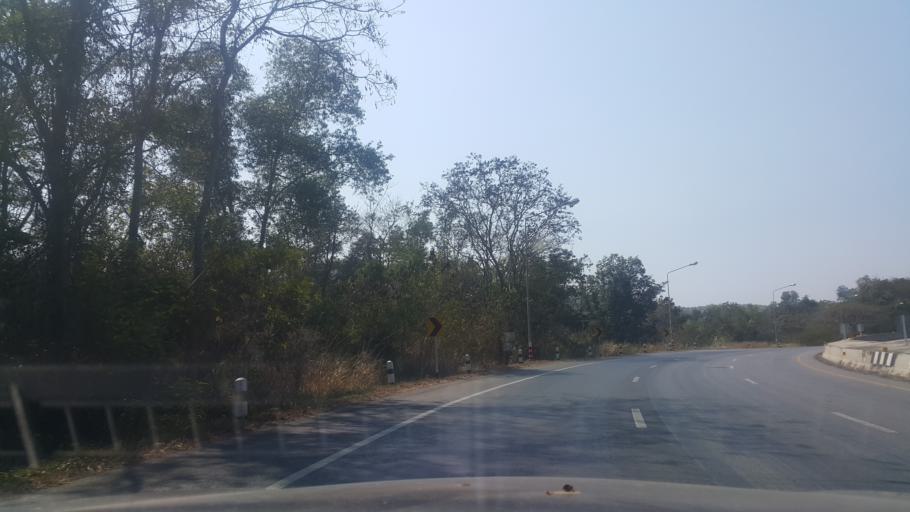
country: TH
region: Nakhon Ratchasima
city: Wang Nam Khiao
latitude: 14.4599
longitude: 101.9053
